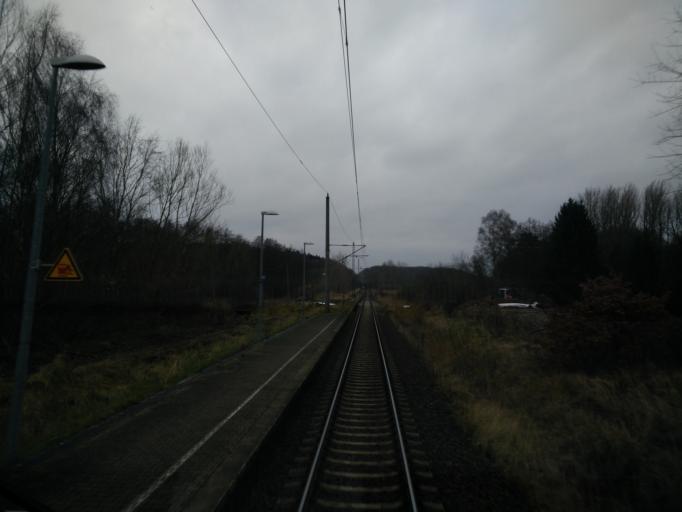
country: DE
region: Mecklenburg-Vorpommern
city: Bad Kleinen
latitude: 53.8063
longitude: 11.4820
